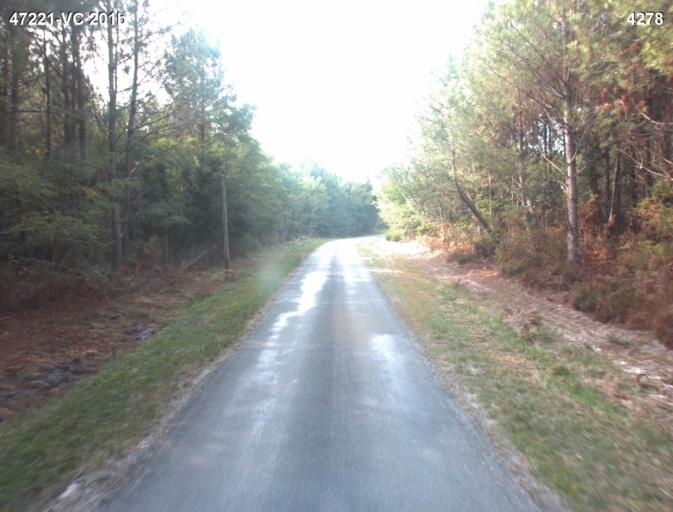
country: FR
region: Aquitaine
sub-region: Departement du Lot-et-Garonne
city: Mezin
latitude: 44.0899
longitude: 0.2022
